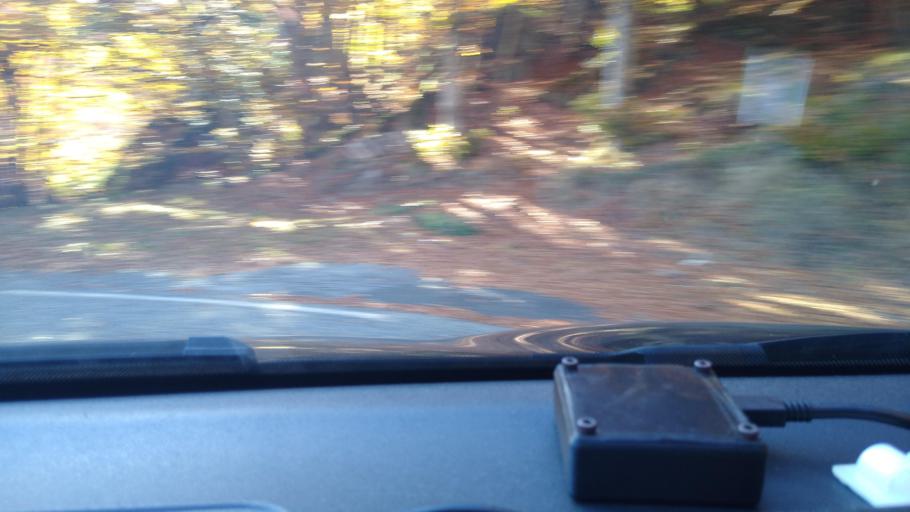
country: FR
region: Midi-Pyrenees
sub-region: Departement de l'Ariege
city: Ax-les-Thermes
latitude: 42.7290
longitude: 2.0030
